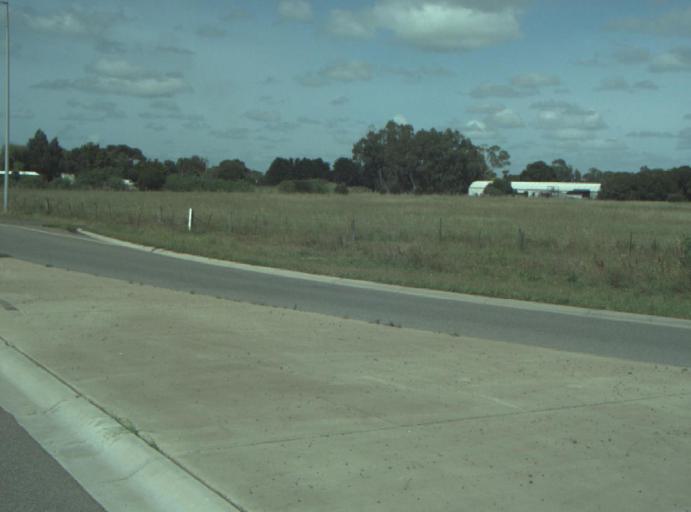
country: AU
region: Victoria
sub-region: Greater Geelong
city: Lara
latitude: -38.0330
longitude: 144.4318
